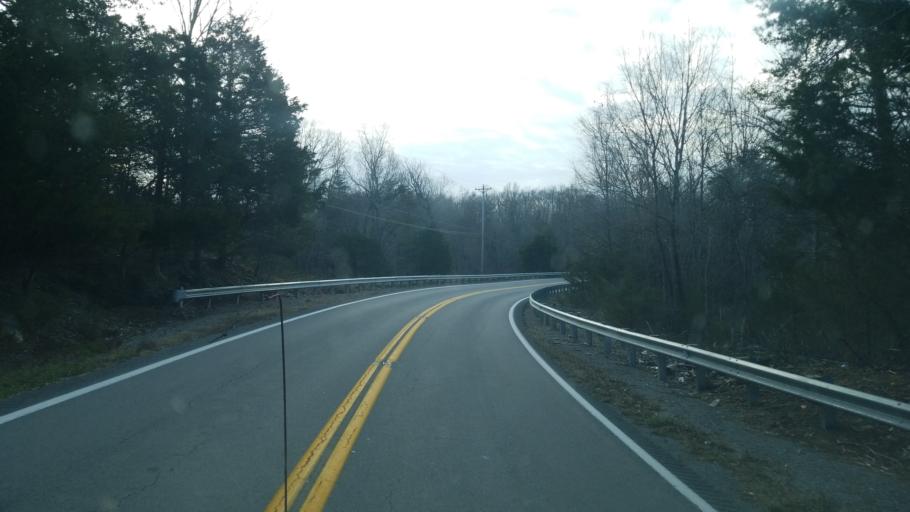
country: US
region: Kentucky
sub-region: Russell County
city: Jamestown
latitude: 36.8702
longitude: -85.1206
